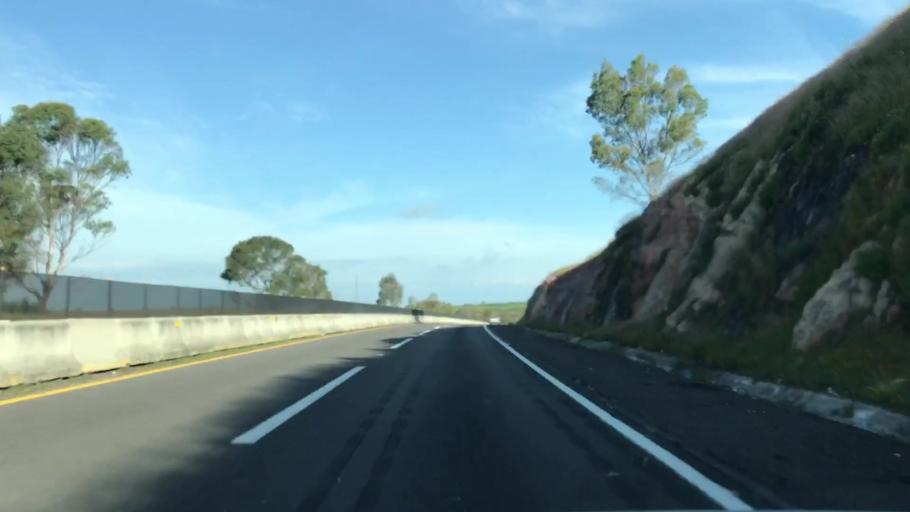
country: MX
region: Jalisco
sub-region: Lagos de Moreno
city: Cristeros [Fraccionamiento]
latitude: 21.3727
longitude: -102.1336
